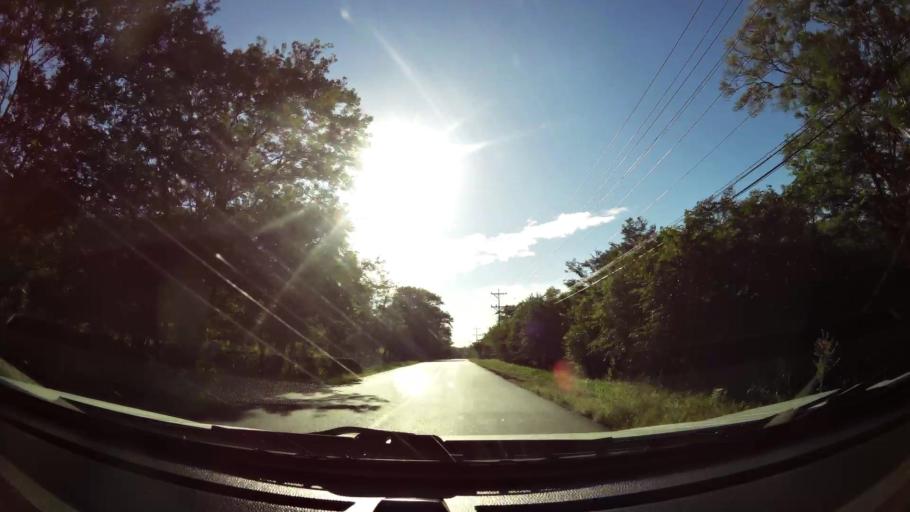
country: CR
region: Guanacaste
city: Sardinal
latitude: 10.5305
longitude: -85.6602
